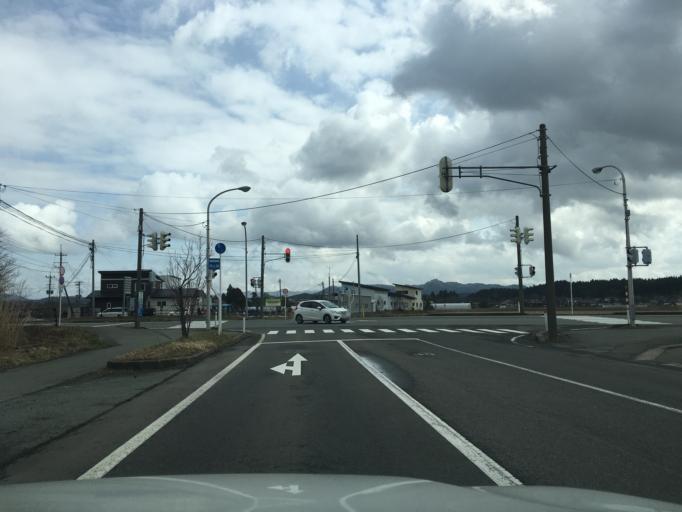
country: JP
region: Akita
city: Tenno
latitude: 39.9392
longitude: 140.1113
